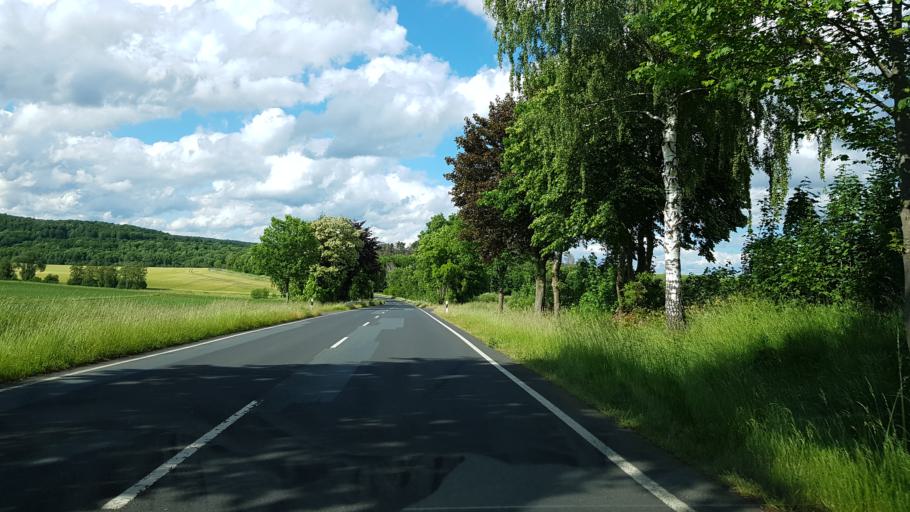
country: DE
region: Lower Saxony
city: Moringen
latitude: 51.7088
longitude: 9.8746
